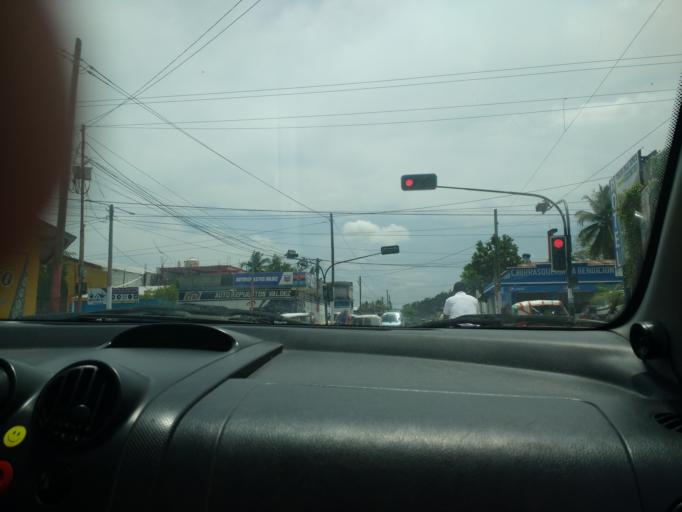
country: GT
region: Peten
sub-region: Municipio de San Benito
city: San Benito
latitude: 16.9174
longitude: -89.9085
